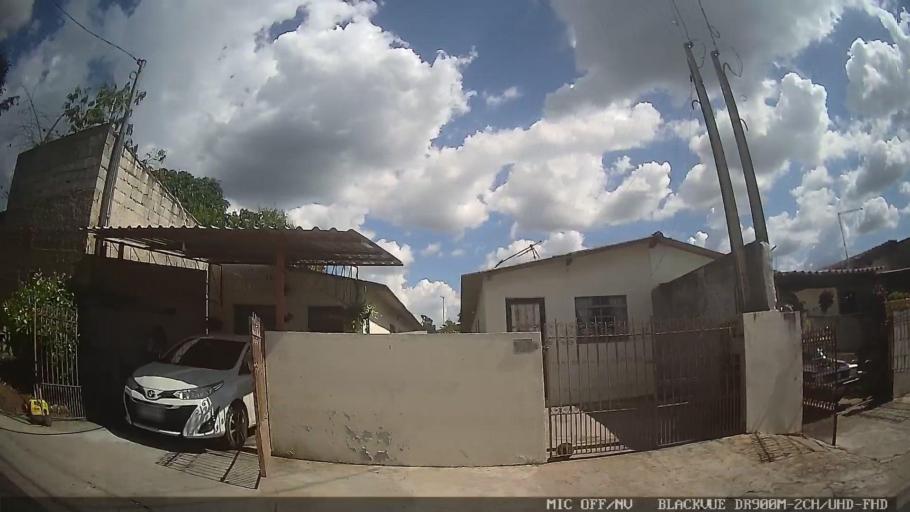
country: BR
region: Sao Paulo
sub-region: Atibaia
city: Atibaia
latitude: -23.1487
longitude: -46.5627
